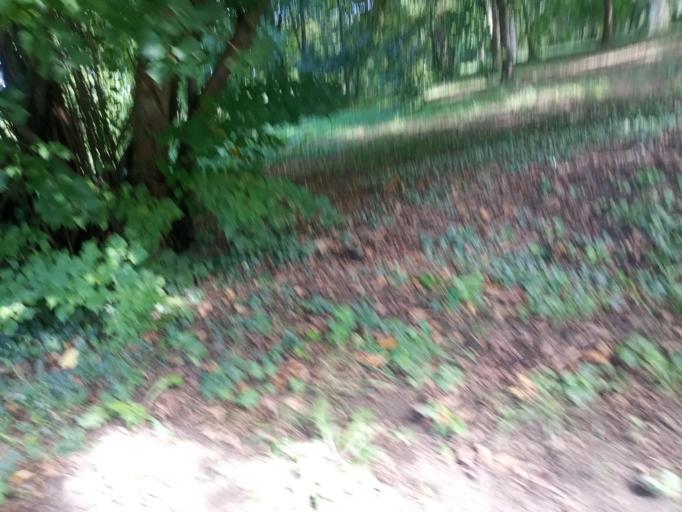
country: HU
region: Veszprem
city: Osi
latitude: 47.1361
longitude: 18.2463
